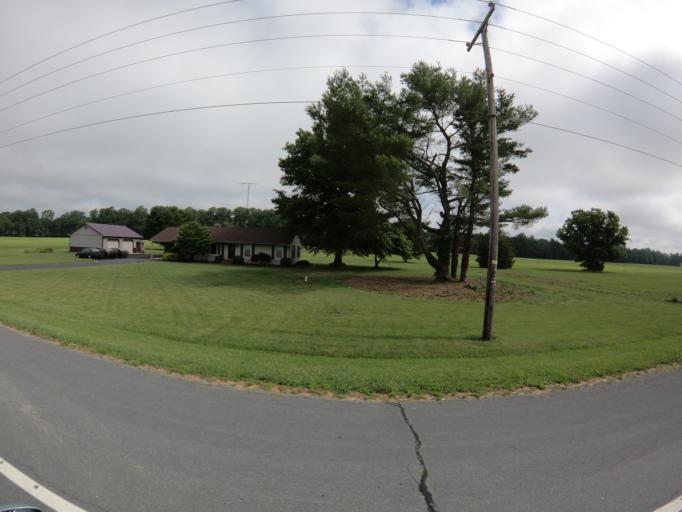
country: US
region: Delaware
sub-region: Kent County
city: Felton
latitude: 39.0058
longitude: -75.5457
